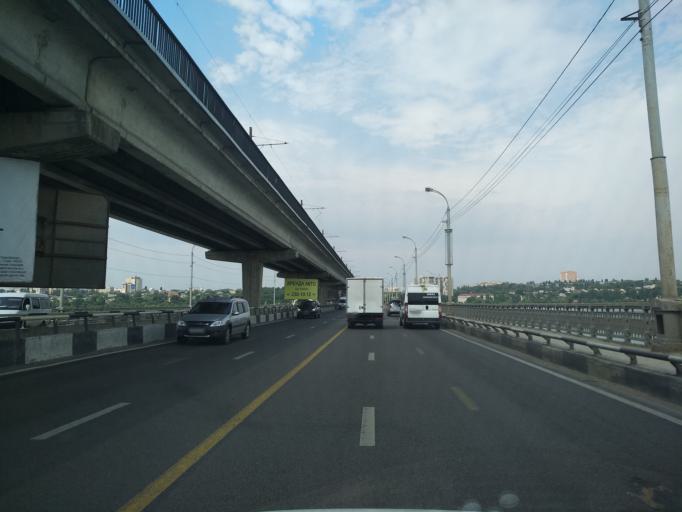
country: RU
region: Voronezj
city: Voronezh
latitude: 51.6898
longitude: 39.2479
